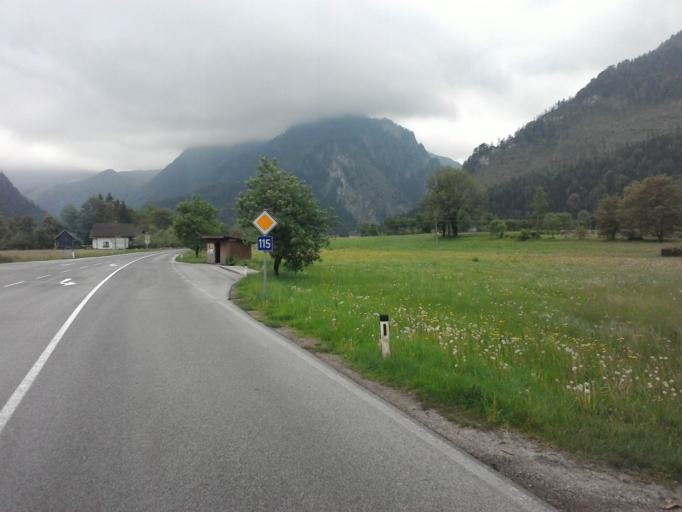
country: AT
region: Styria
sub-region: Politischer Bezirk Liezen
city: Gams bei Hieflau
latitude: 47.6450
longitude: 14.7555
